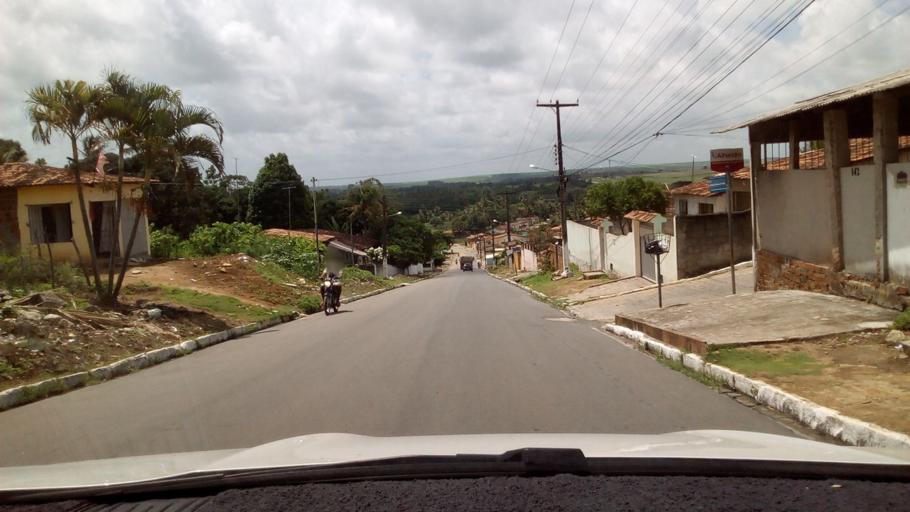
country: BR
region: Paraiba
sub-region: Alhandra
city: Alhandra
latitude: -7.4381
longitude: -34.9130
